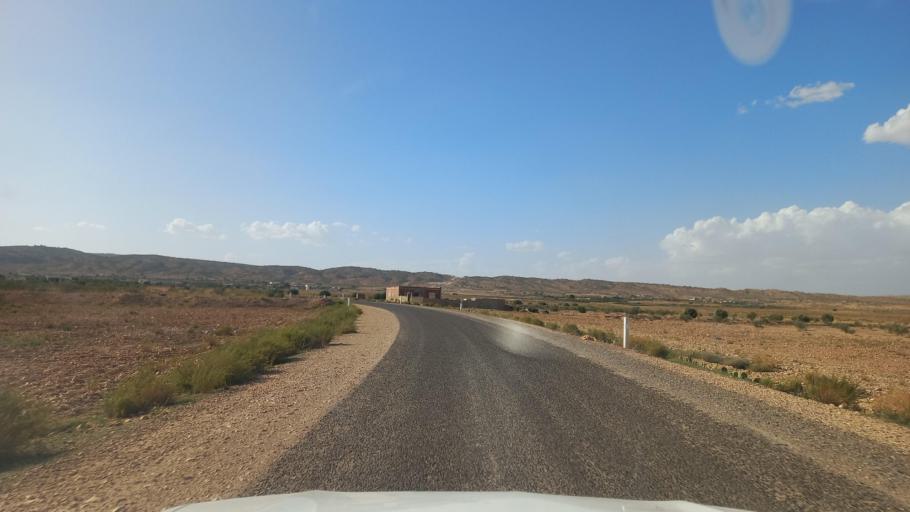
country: TN
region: Al Qasrayn
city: Sbiba
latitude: 35.3381
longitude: 8.9991
